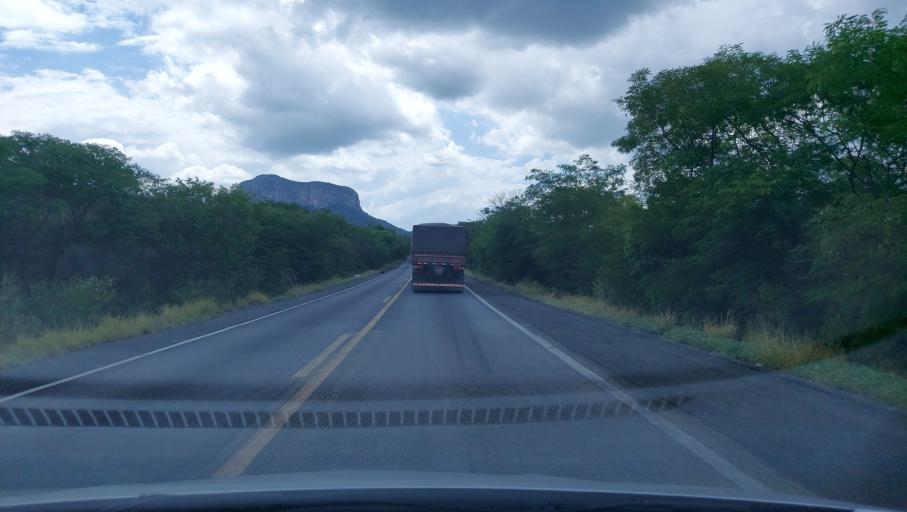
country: BR
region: Bahia
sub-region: Oliveira Dos Brejinhos
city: Beira Rio
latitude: -12.3935
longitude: -42.4020
